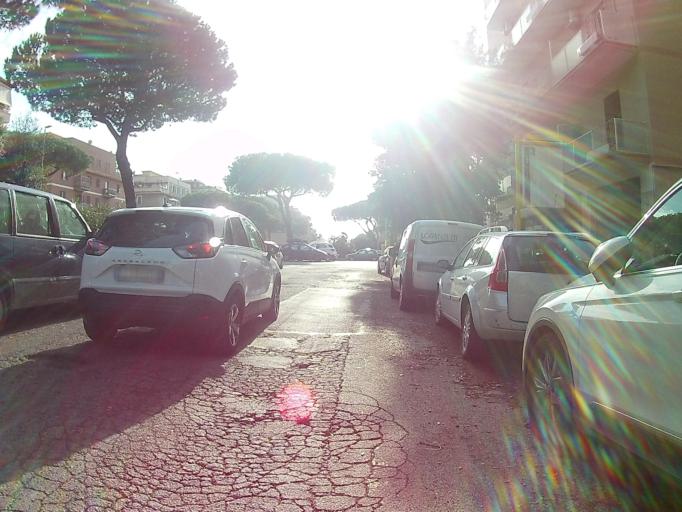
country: IT
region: Latium
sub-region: Citta metropolitana di Roma Capitale
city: Lido di Ostia
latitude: 41.7327
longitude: 12.2900
